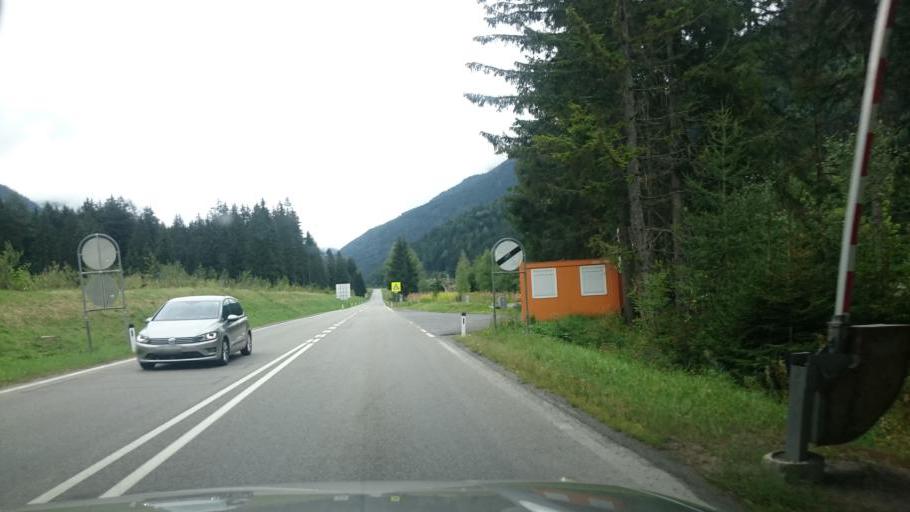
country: AT
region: Tyrol
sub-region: Politischer Bezirk Landeck
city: Sankt Anton am Arlberg
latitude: 47.1436
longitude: 10.3146
